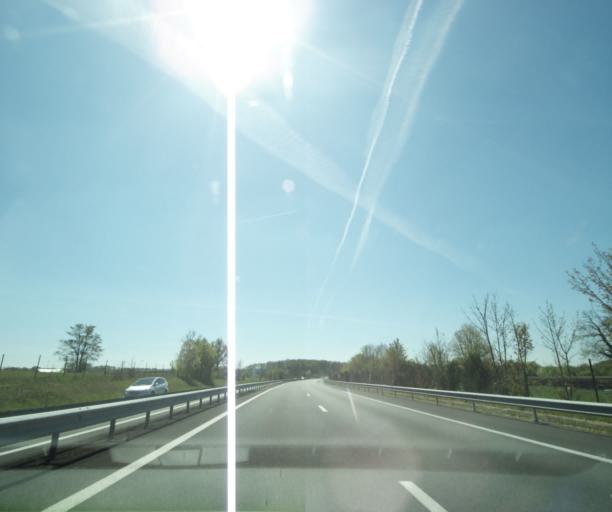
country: FR
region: Limousin
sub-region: Departement de la Haute-Vienne
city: Saint-Sulpice-les-Feuilles
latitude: 46.3150
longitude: 1.4184
